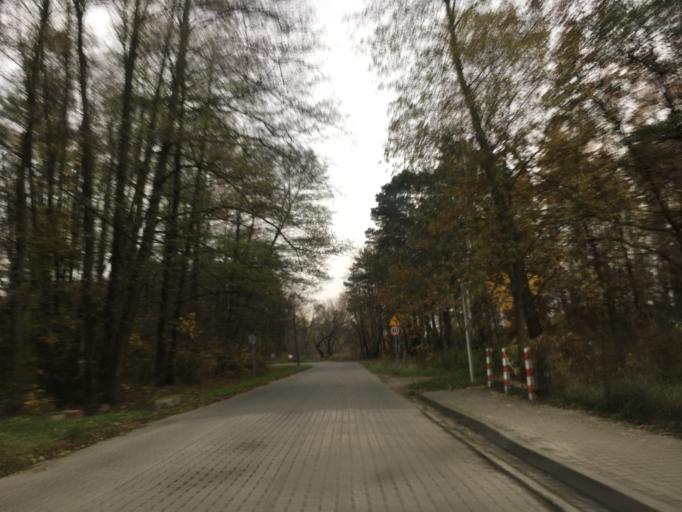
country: PL
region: Masovian Voivodeship
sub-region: Powiat piaseczynski
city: Lesznowola
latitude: 52.0435
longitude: 20.9351
